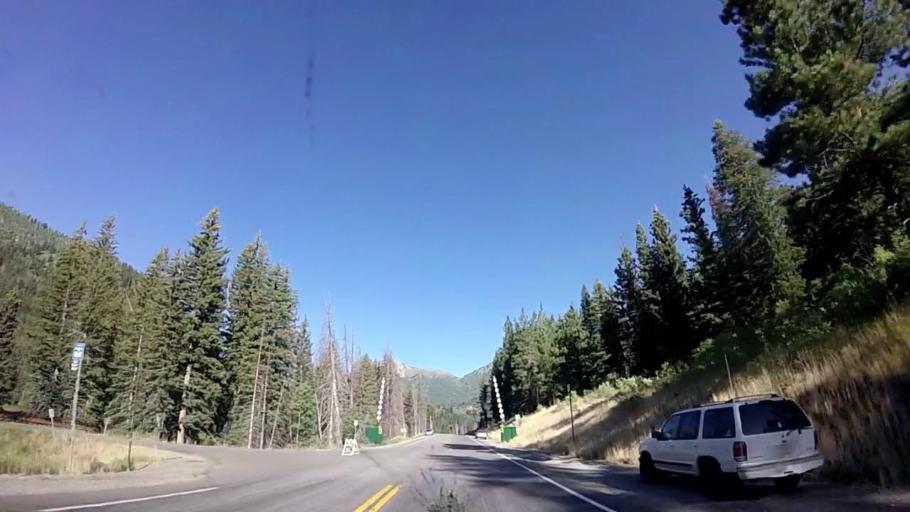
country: US
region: Utah
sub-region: Summit County
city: Summit Park
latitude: 40.6428
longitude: -111.6364
